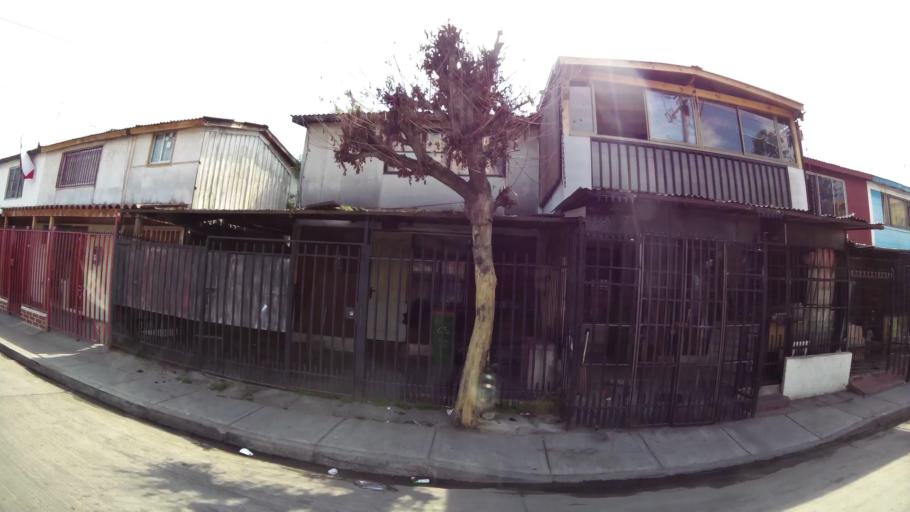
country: CL
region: Santiago Metropolitan
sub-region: Provincia de Santiago
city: La Pintana
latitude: -33.5912
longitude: -70.6037
